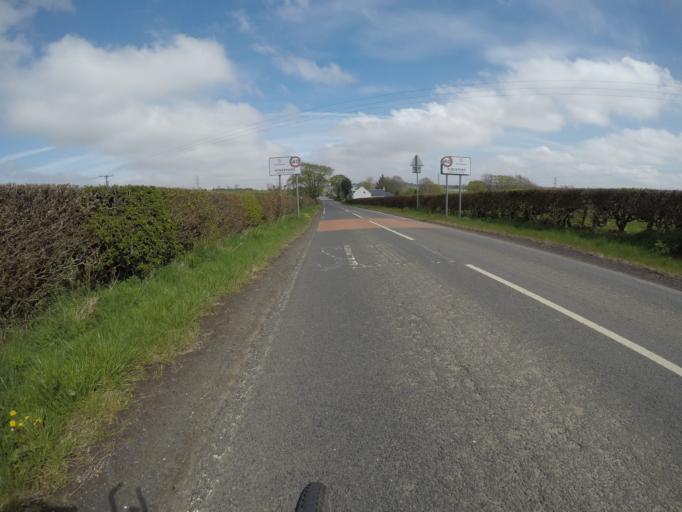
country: GB
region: Scotland
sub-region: East Ayrshire
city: Stewarton
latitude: 55.7014
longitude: -4.4804
